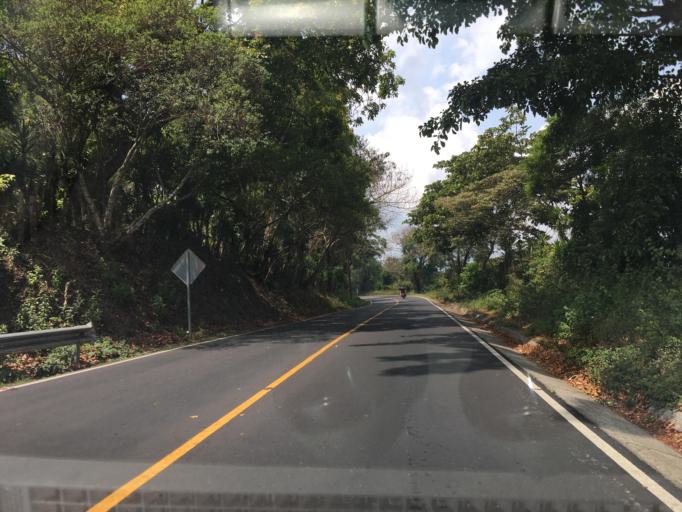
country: GT
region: Guatemala
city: Villa Canales
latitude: 14.4154
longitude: -90.5302
